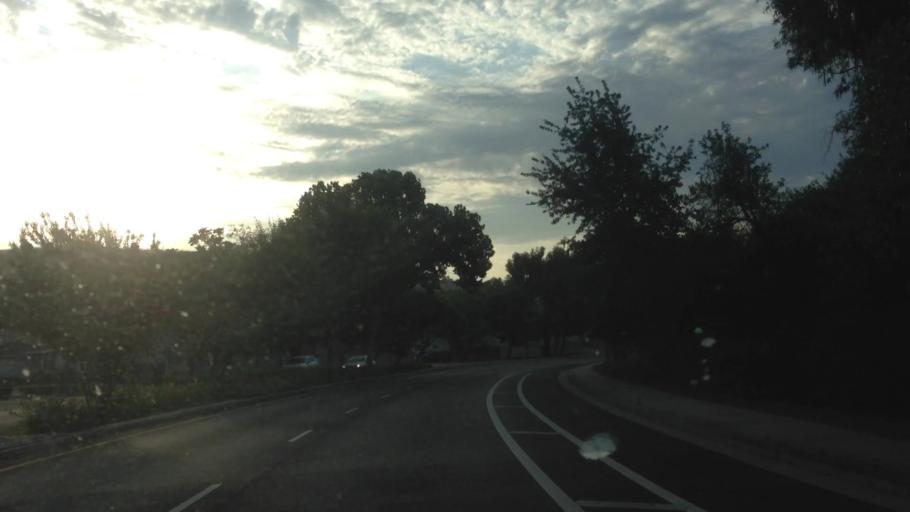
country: US
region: California
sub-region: Santa Clara County
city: Seven Trees
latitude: 37.2978
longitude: -121.7963
